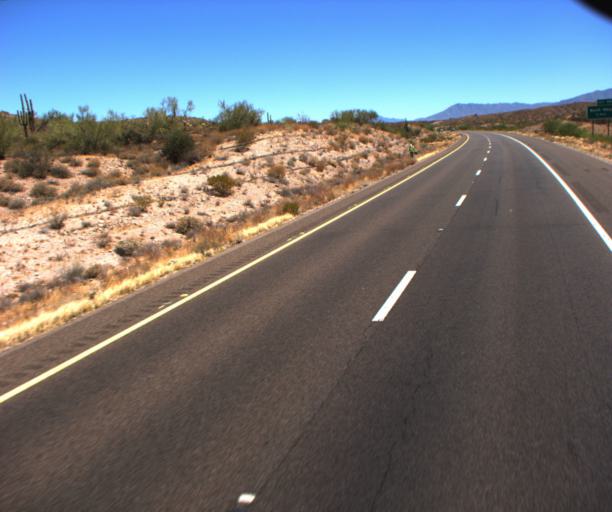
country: US
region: Arizona
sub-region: Maricopa County
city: Fountain Hills
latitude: 33.6109
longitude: -111.5739
